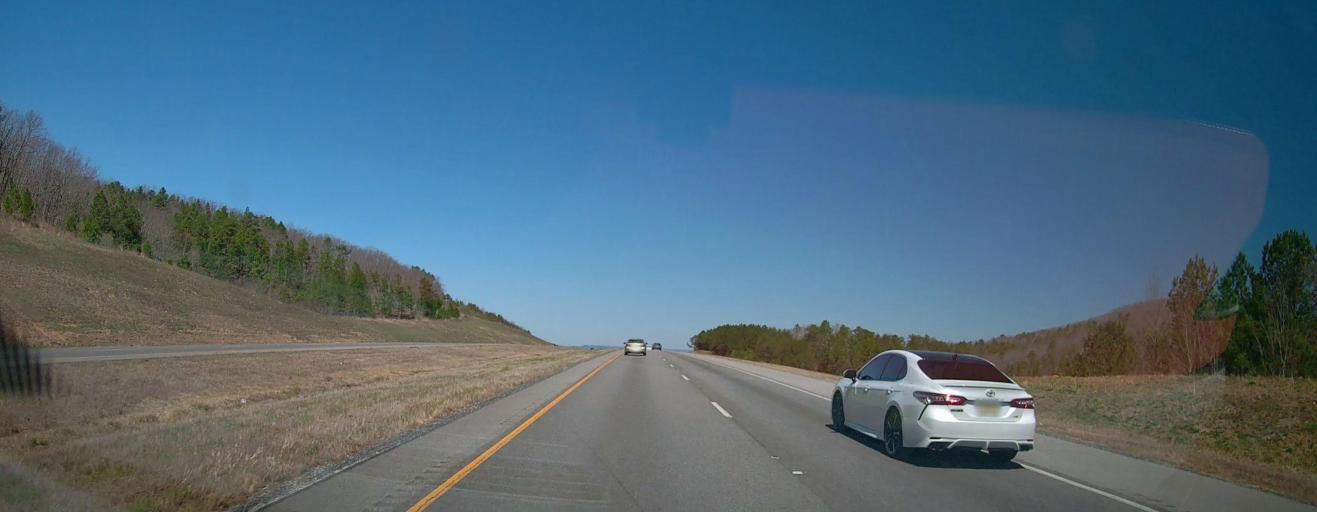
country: US
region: Alabama
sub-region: Calhoun County
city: Anniston
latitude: 33.6830
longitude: -85.8029
